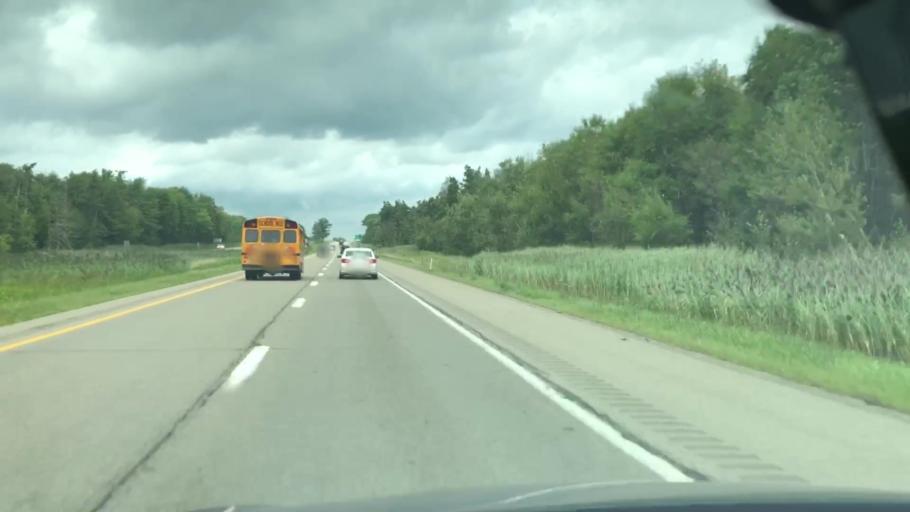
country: US
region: Pennsylvania
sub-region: Erie County
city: Edinboro
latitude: 41.8679
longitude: -80.1763
